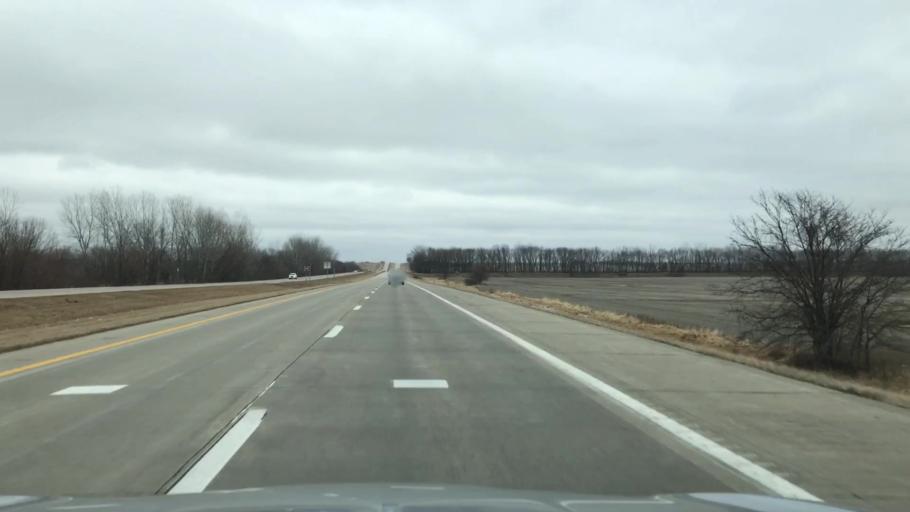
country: US
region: Missouri
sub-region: Livingston County
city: Chillicothe
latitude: 39.7767
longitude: -93.4235
